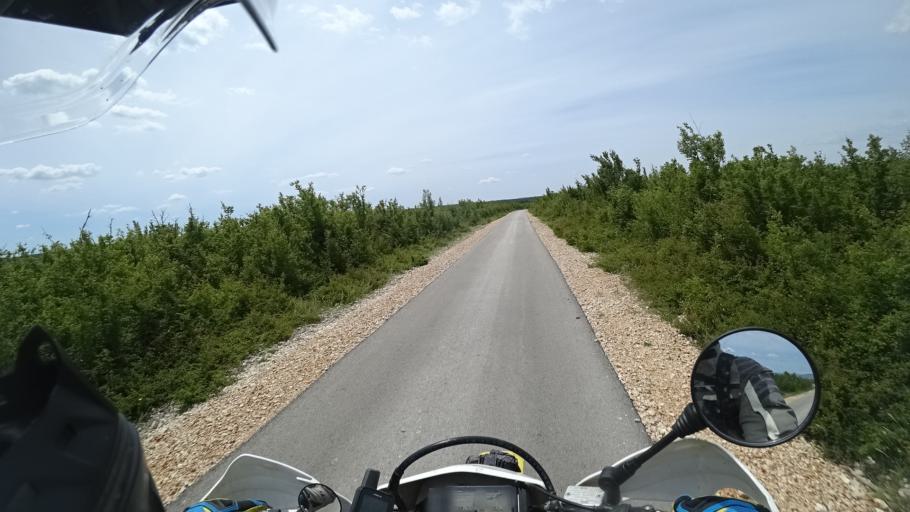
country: HR
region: Sibensko-Kniniska
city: Kistanje
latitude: 44.0724
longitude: 15.9810
